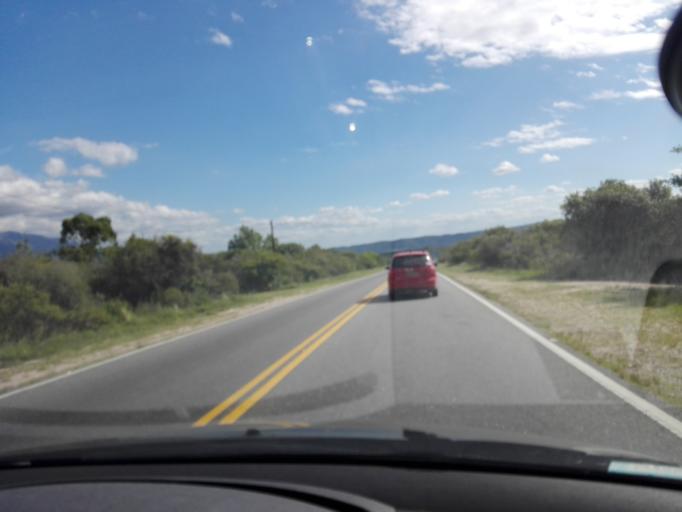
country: AR
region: Cordoba
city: Mina Clavero
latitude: -31.7617
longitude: -64.9630
